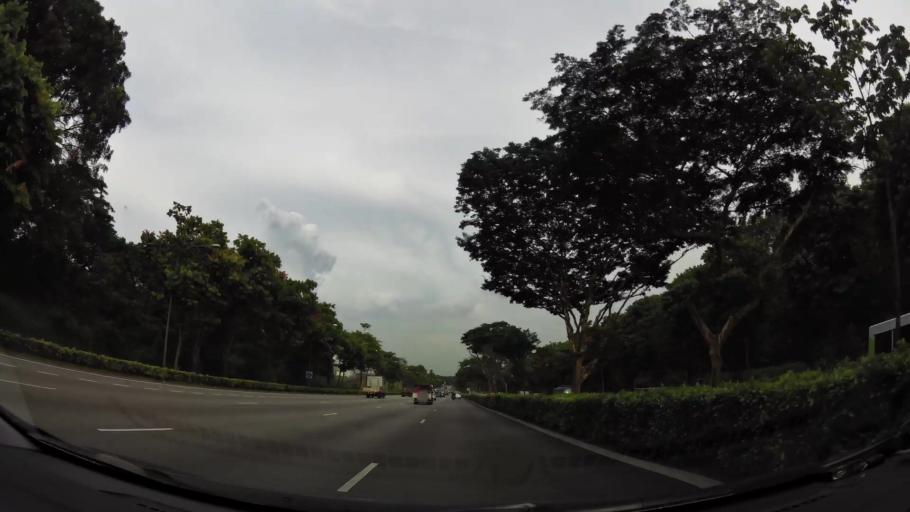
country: MY
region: Johor
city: Johor Bahru
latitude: 1.3681
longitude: 103.7140
